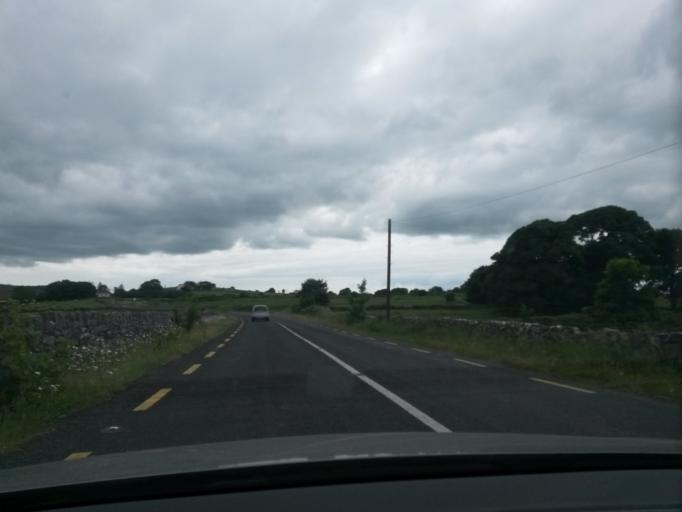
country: IE
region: Munster
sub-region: An Clar
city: Ennis
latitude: 52.9912
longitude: -9.2019
